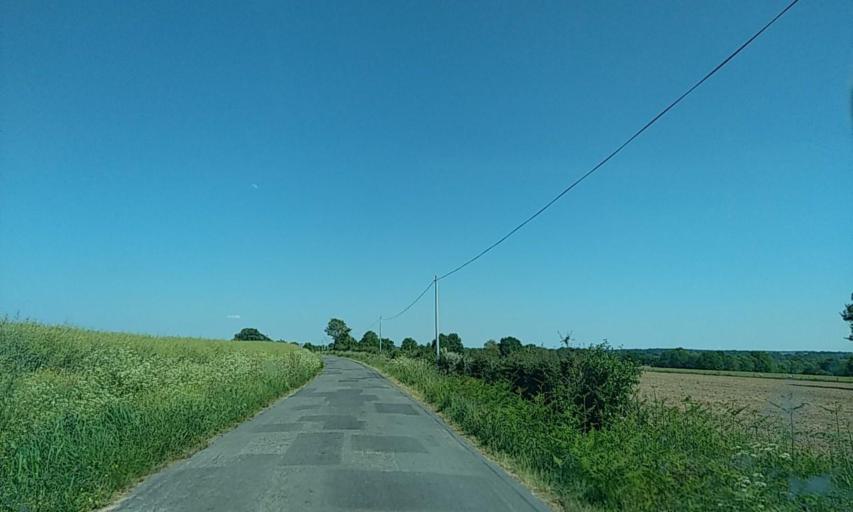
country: FR
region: Poitou-Charentes
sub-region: Departement des Deux-Sevres
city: La Chapelle-Saint-Laurent
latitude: 46.7700
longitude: -0.4727
